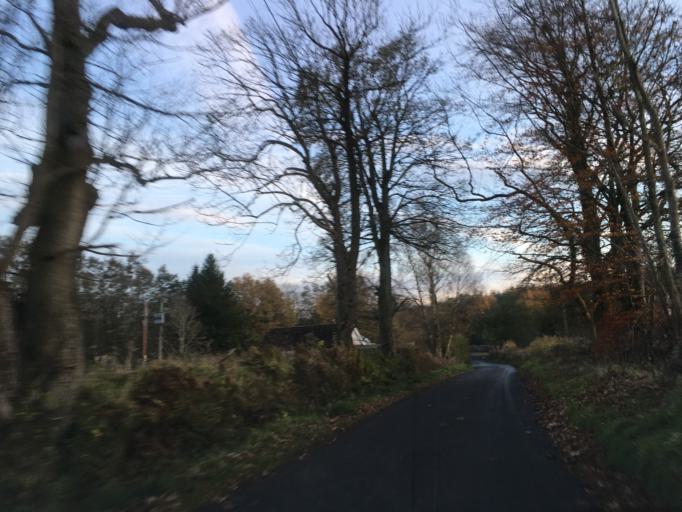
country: GB
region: Scotland
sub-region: Fife
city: Saline
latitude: 56.1235
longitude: -3.5865
